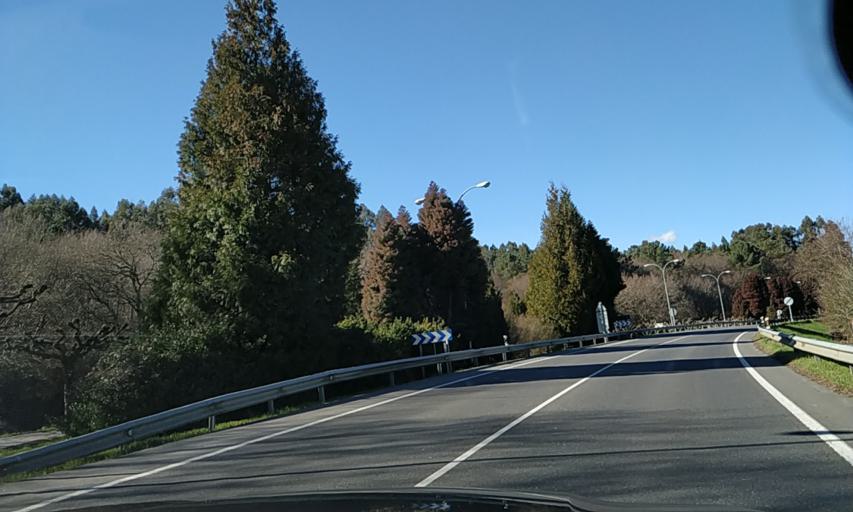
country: ES
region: Galicia
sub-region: Provincia de Pontevedra
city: Silleda
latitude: 42.6869
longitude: -8.2192
